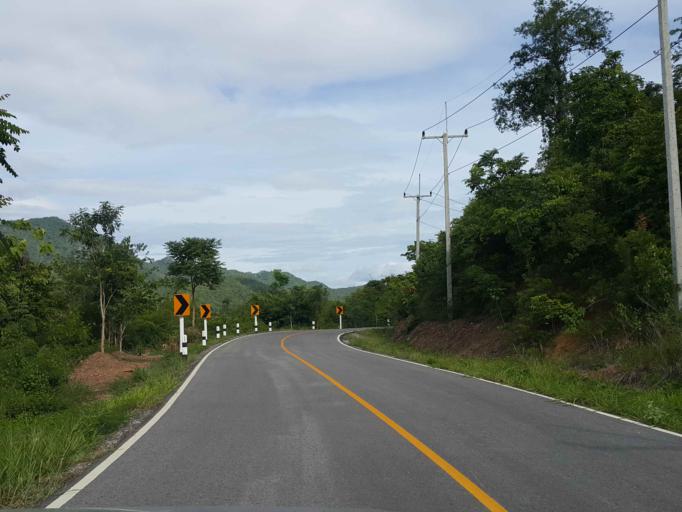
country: TH
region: Sukhothai
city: Thung Saliam
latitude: 17.2414
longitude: 99.4948
